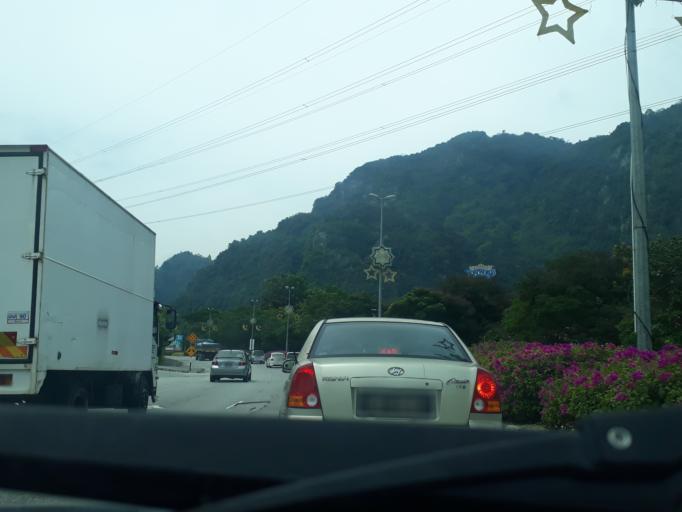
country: MY
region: Perak
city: Ipoh
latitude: 4.6244
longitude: 101.1517
